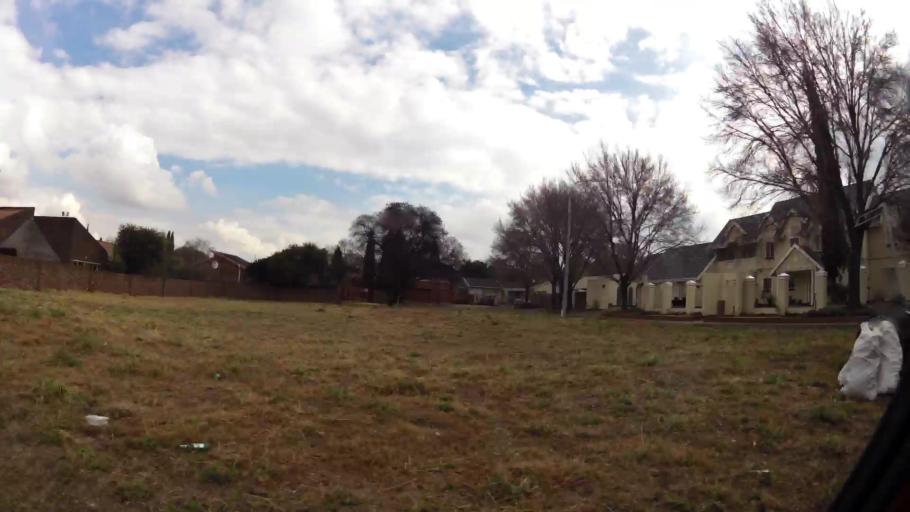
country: ZA
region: Gauteng
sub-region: Sedibeng District Municipality
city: Vanderbijlpark
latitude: -26.7394
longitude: 27.8529
